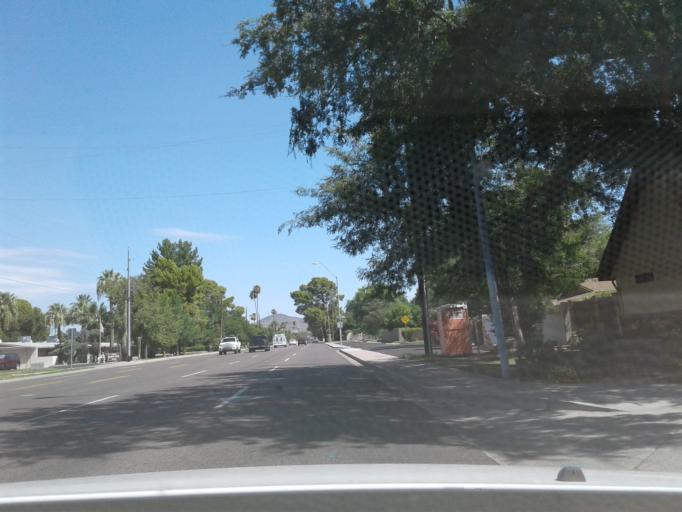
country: US
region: Arizona
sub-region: Maricopa County
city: Phoenix
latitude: 33.5431
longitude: -112.0824
